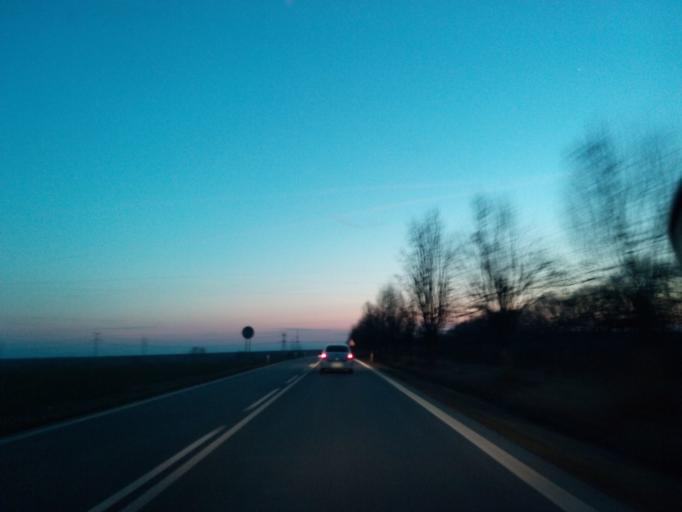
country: SK
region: Kosicky
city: Michalovce
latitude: 48.7164
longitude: 21.8413
